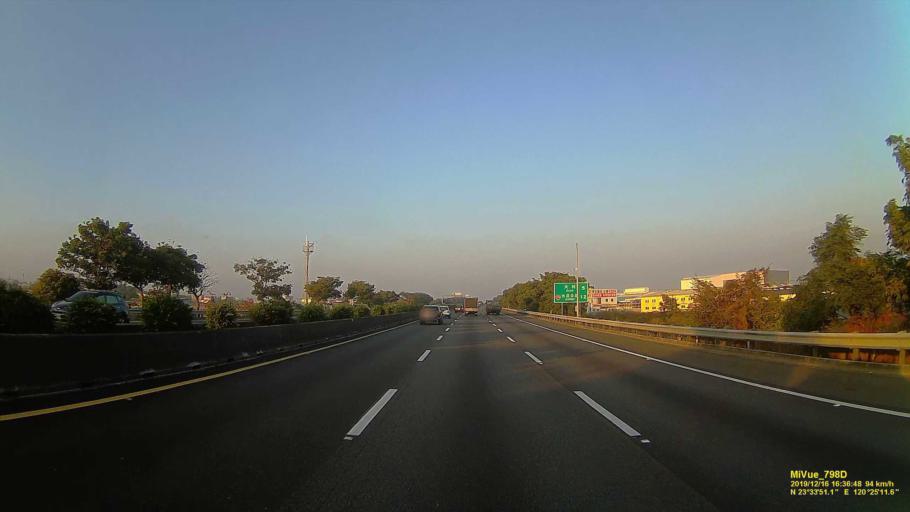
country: TW
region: Taiwan
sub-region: Chiayi
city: Jiayi Shi
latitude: 23.5647
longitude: 120.4201
